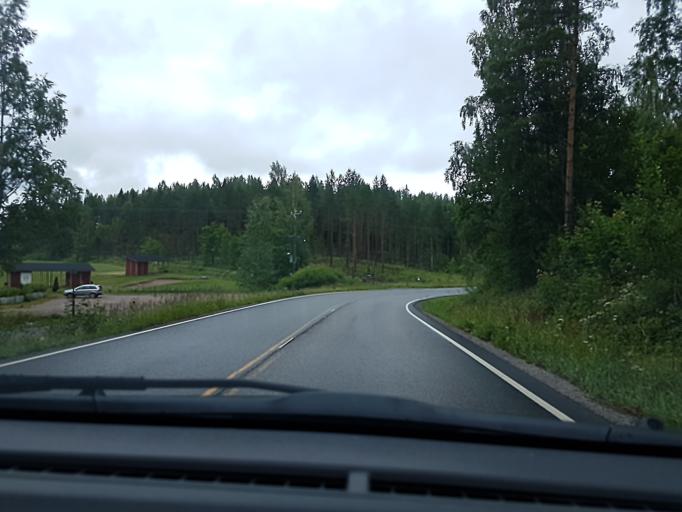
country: FI
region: Uusimaa
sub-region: Helsinki
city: Pornainen
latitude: 60.4467
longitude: 25.3808
